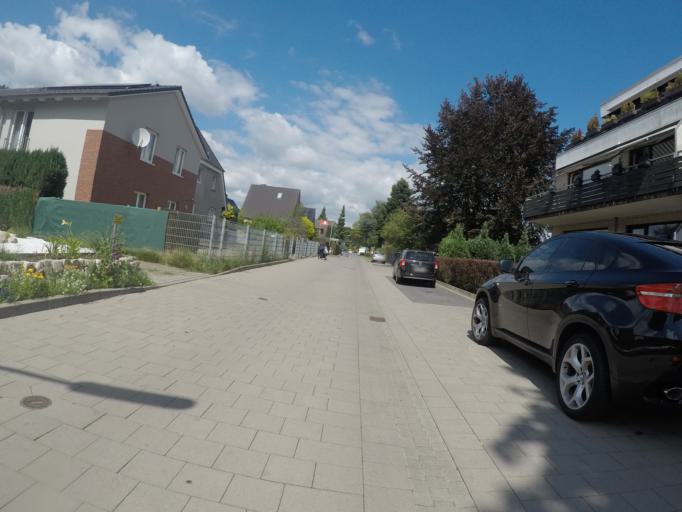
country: DE
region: Hamburg
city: Wandsbek
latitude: 53.5446
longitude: 10.1090
